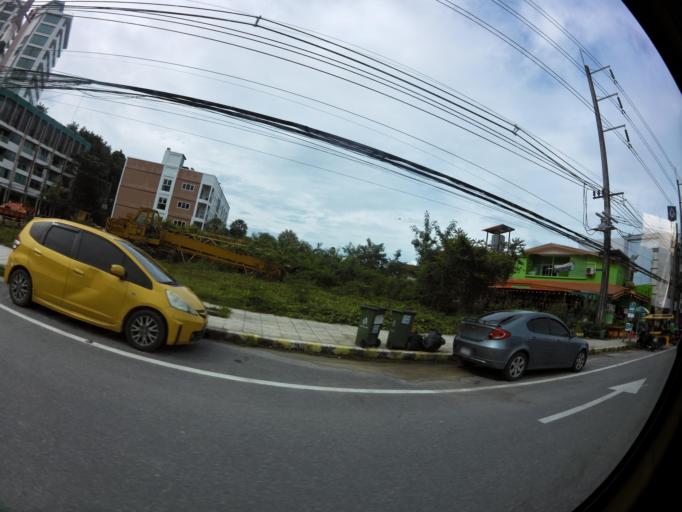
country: TH
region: Phuket
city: Patong
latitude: 7.9467
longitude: 98.2794
